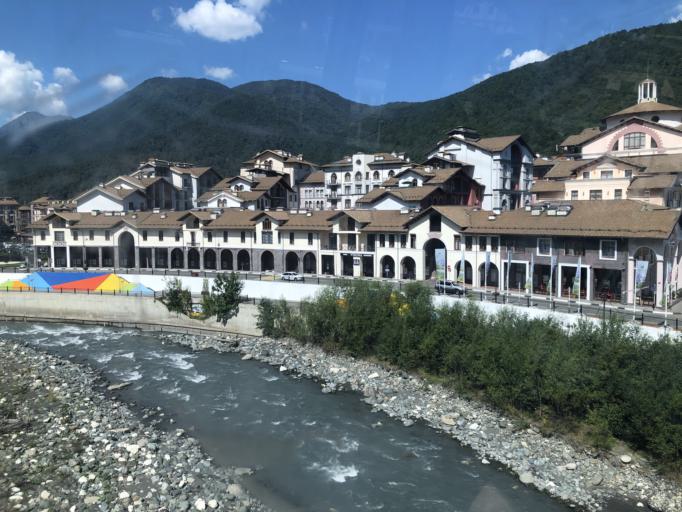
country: RU
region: Krasnodarskiy
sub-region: Sochi City
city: Krasnaya Polyana
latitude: 43.6822
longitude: 40.2663
